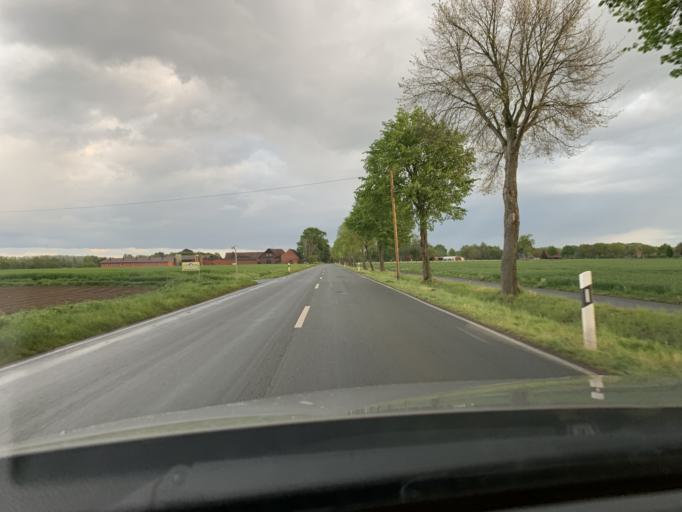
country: DE
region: North Rhine-Westphalia
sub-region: Regierungsbezirk Detmold
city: Langenberg
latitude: 51.7944
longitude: 8.3706
